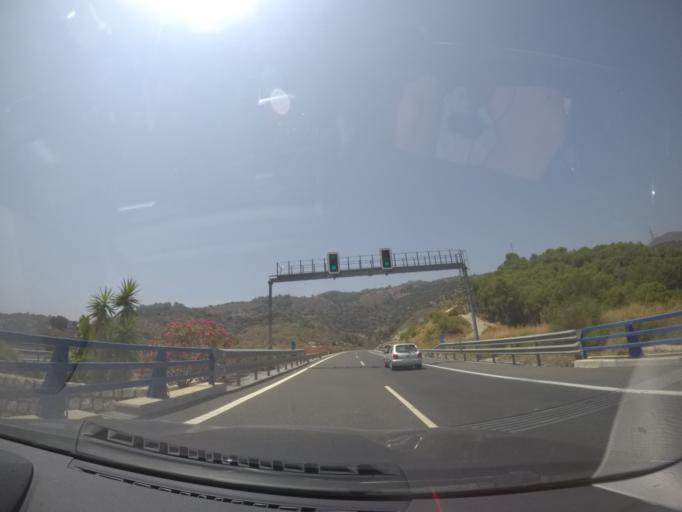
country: ES
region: Andalusia
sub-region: Provincia de Granada
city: Almunecar
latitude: 36.7628
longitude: -3.7025
